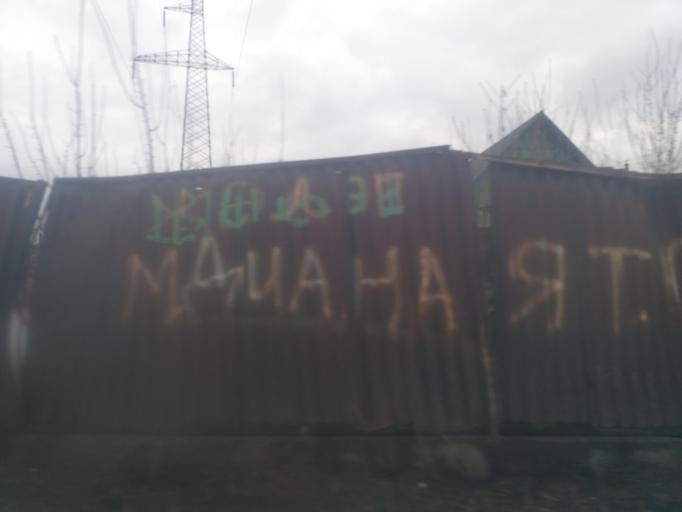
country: KZ
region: Almaty Oblysy
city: Burunday
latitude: 43.2170
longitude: 76.7500
